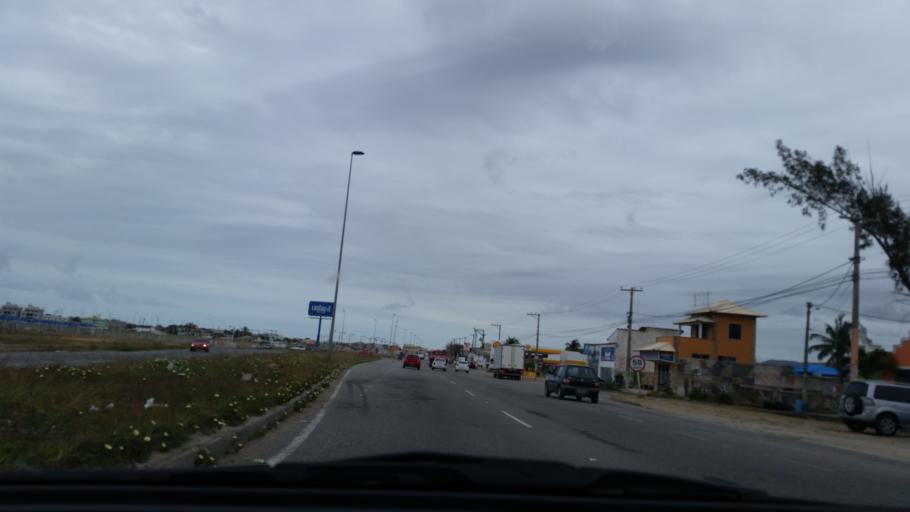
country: BR
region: Rio de Janeiro
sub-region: Sao Pedro Da Aldeia
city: Sao Pedro da Aldeia
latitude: -22.8304
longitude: -42.0905
